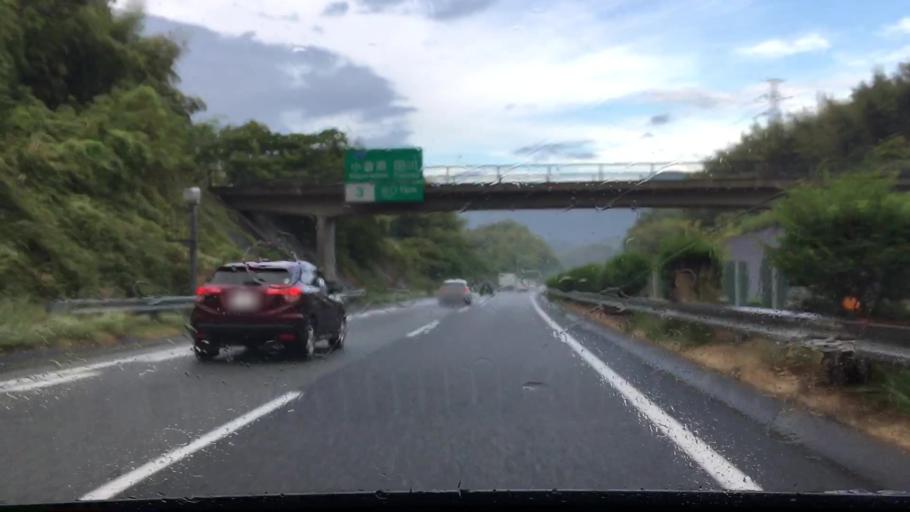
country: JP
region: Fukuoka
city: Kitakyushu
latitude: 33.8081
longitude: 130.8414
